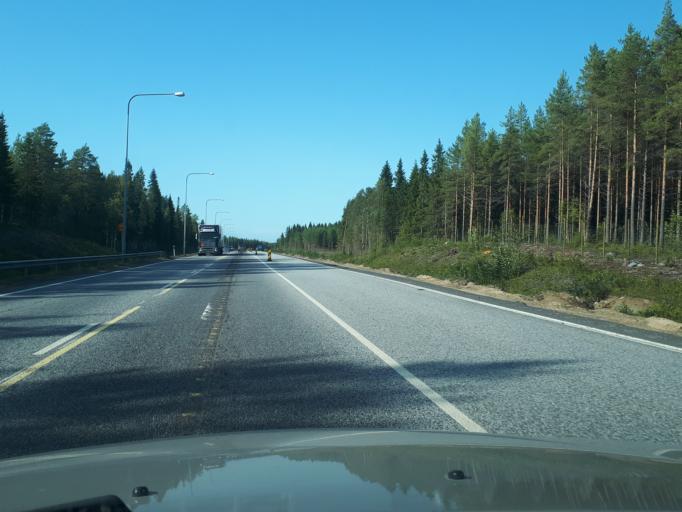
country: FI
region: Northern Ostrobothnia
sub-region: Oulunkaari
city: Ii
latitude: 65.2580
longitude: 25.3708
